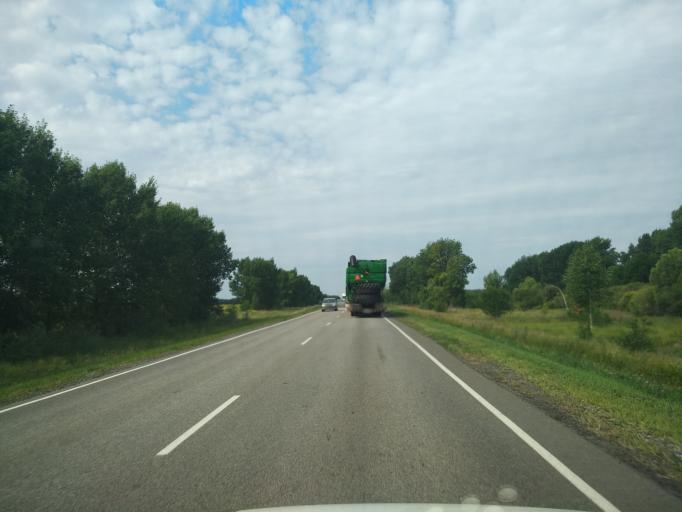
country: RU
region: Voronezj
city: Pereleshinskiy
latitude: 51.8717
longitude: 40.3922
